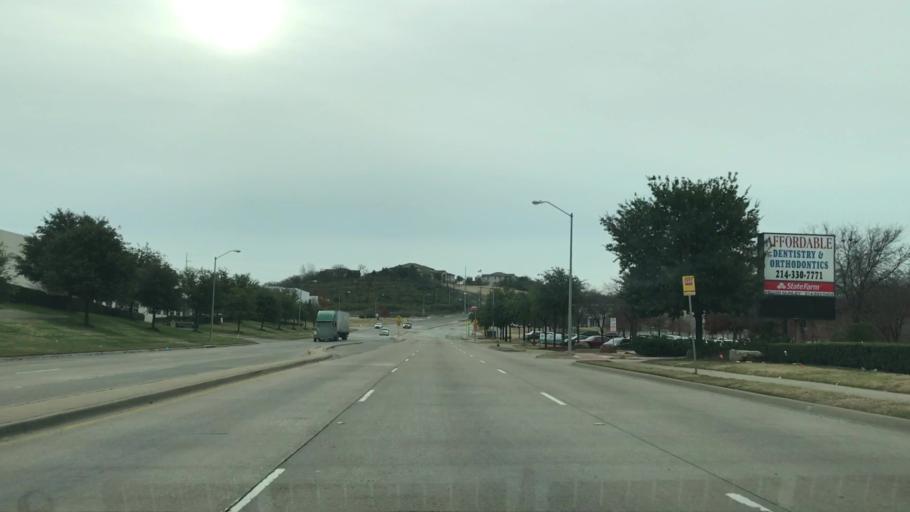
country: US
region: Texas
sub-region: Dallas County
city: Cockrell Hill
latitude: 32.7620
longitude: -96.8947
